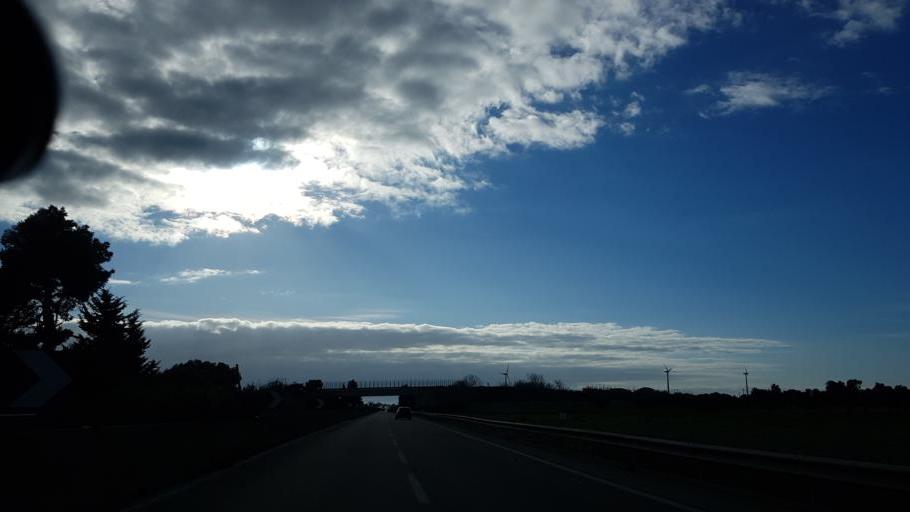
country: IT
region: Apulia
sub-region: Provincia di Brindisi
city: La Rosa
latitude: 40.5784
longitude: 17.9794
